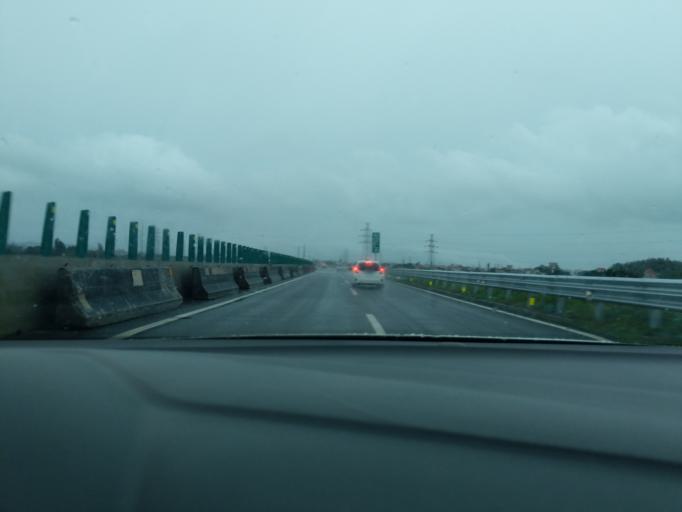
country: CN
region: Guangdong
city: Shuikou
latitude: 22.4647
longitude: 112.7472
